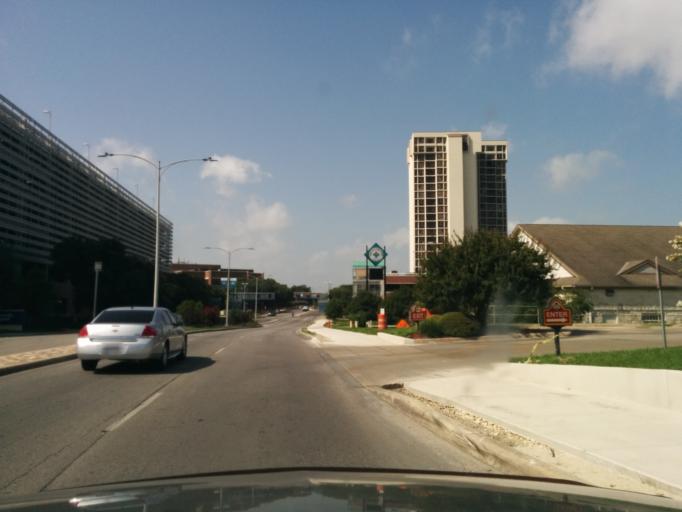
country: US
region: Texas
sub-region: Bexar County
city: Balcones Heights
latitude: 29.5101
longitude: -98.5804
